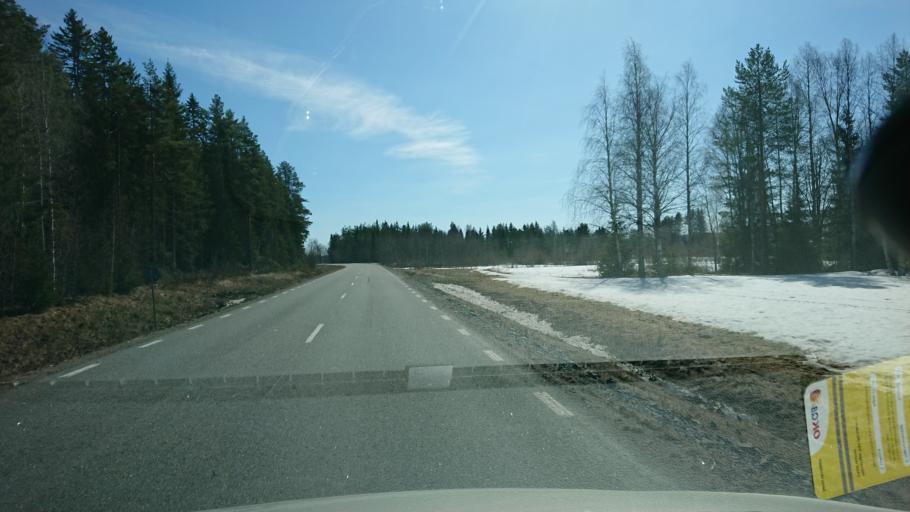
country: SE
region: Vaesternorrland
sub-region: Solleftea Kommun
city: As
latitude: 63.6628
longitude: 16.4455
